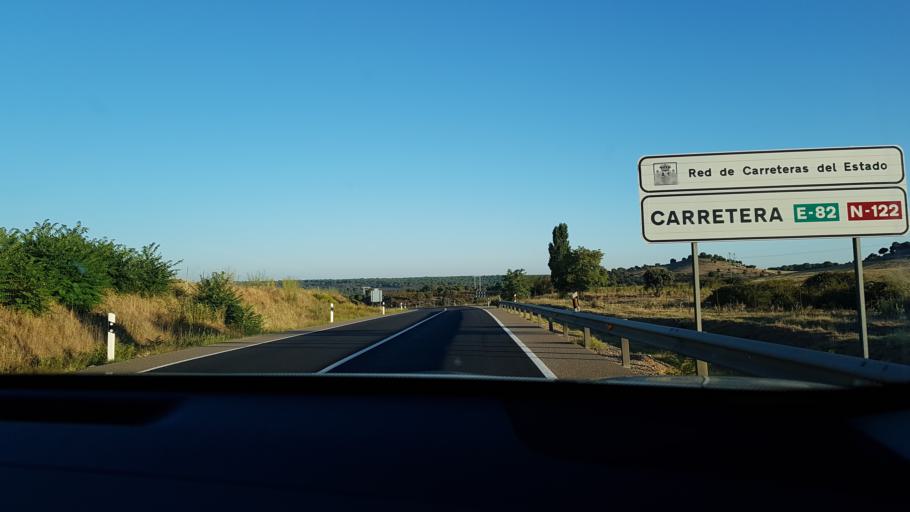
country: ES
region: Castille and Leon
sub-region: Provincia de Zamora
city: Roales
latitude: 41.5274
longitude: -5.8126
